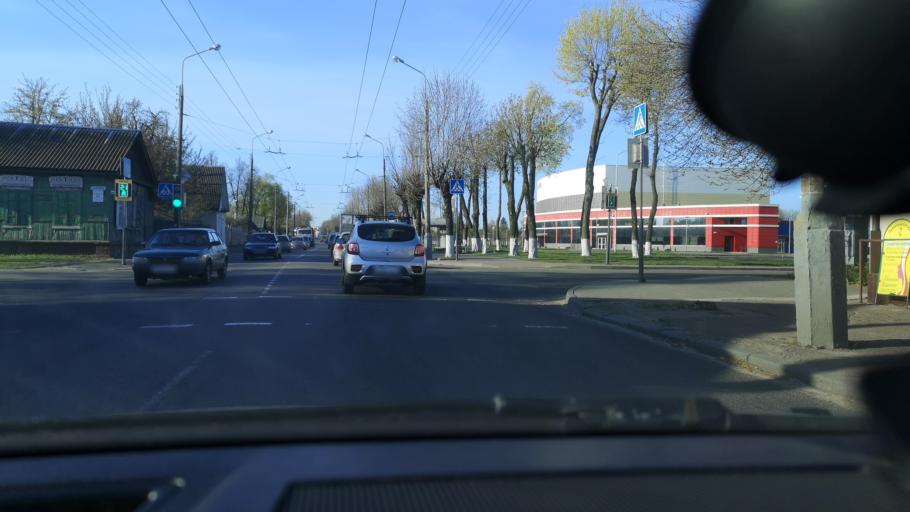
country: BY
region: Gomel
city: Gomel
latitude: 52.4331
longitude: 30.9759
